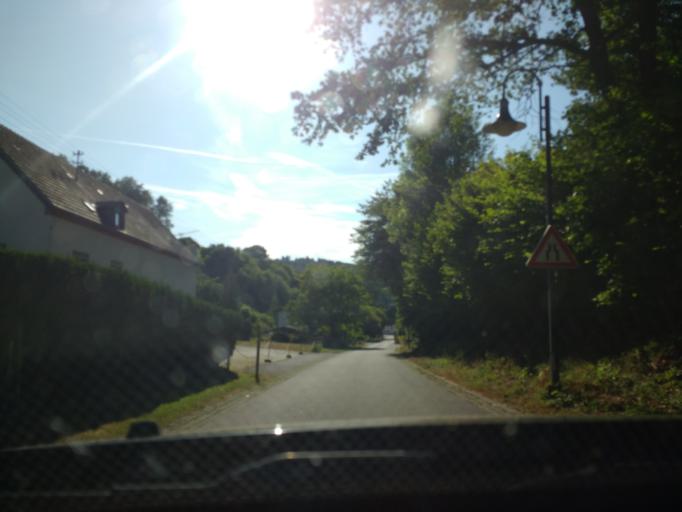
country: DE
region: Rheinland-Pfalz
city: Densborn
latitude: 50.1258
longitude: 6.6081
